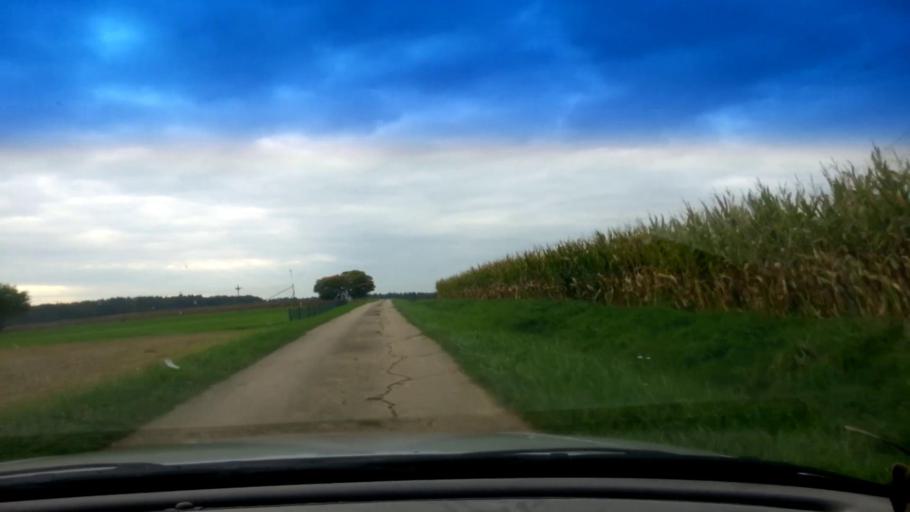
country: DE
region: Bavaria
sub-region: Upper Franconia
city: Memmelsdorf
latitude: 49.9707
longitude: 10.9648
